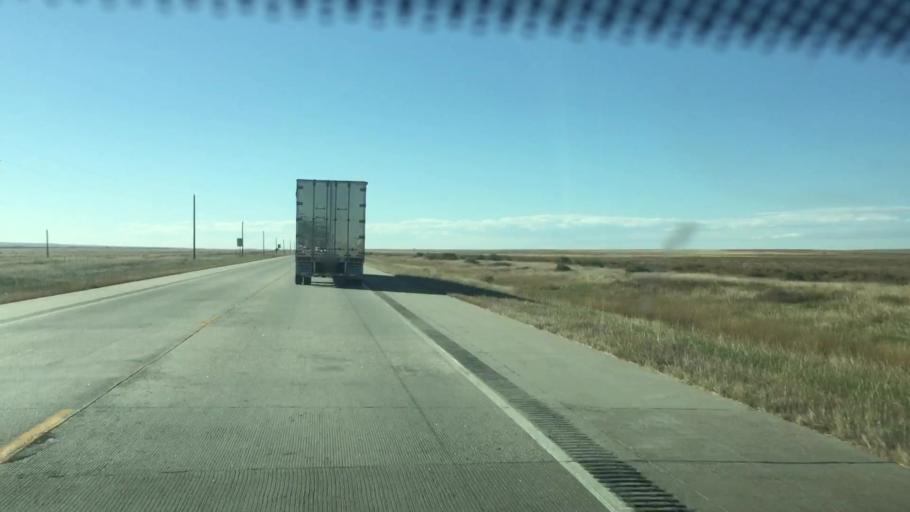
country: US
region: Colorado
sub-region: Kiowa County
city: Eads
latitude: 38.8273
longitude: -103.0219
